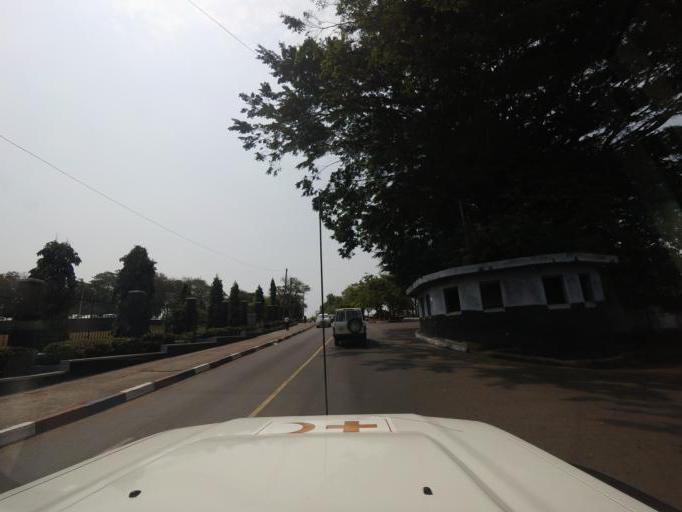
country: LR
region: Montserrado
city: Monrovia
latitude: 6.3025
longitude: -10.7980
